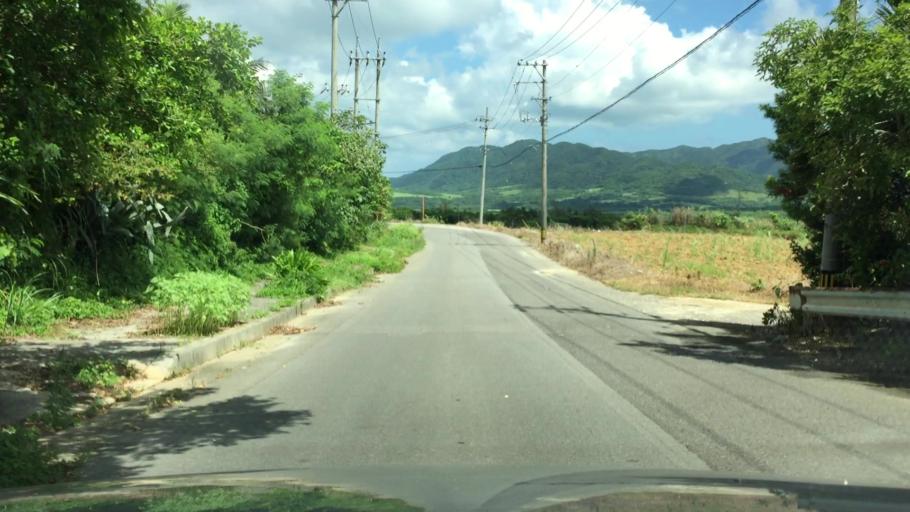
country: JP
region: Okinawa
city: Ishigaki
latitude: 24.3875
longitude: 124.1732
